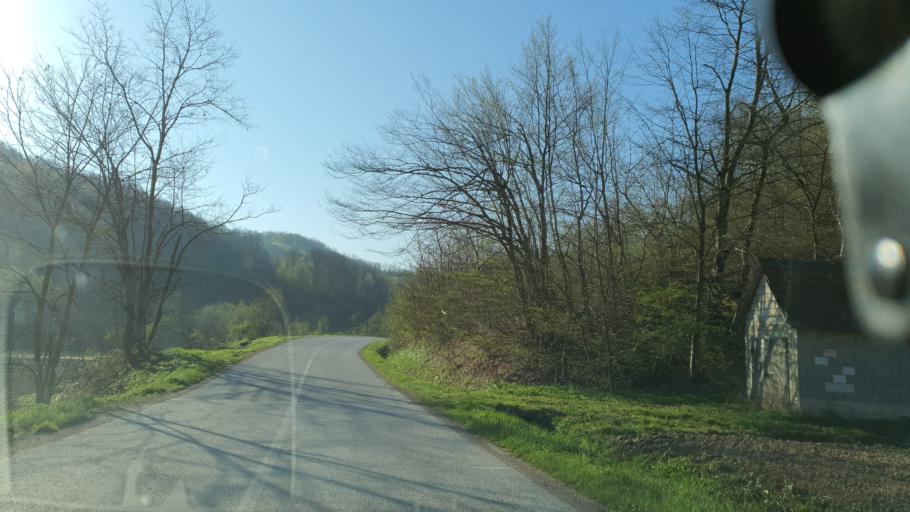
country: RS
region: Central Serbia
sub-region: Kolubarski Okrug
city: Osecina
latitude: 44.3089
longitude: 19.5303
